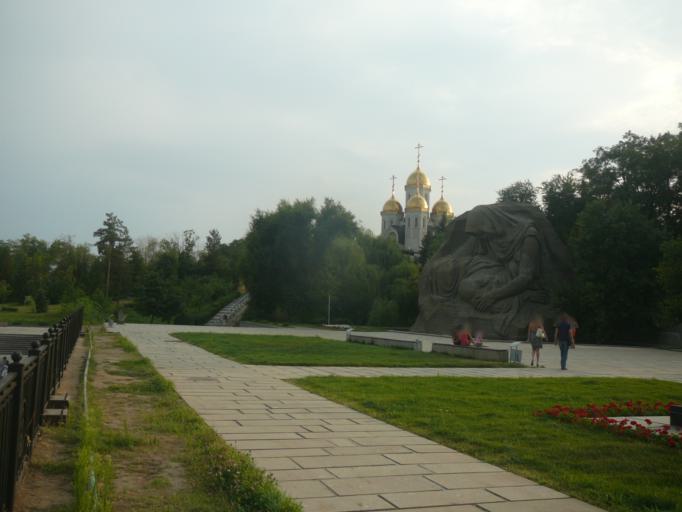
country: RU
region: Volgograd
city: Volgograd
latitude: 48.7417
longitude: 44.5390
